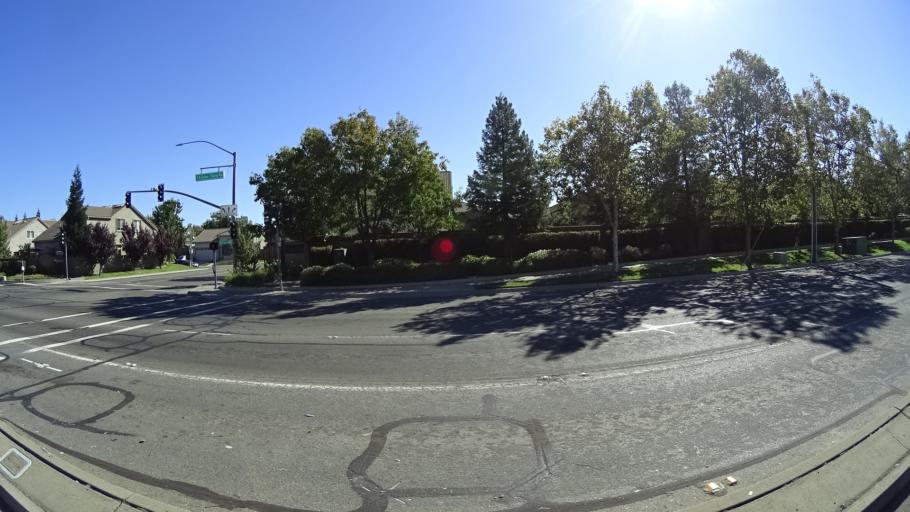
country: US
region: California
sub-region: Sacramento County
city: Vineyard
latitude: 38.4451
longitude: -121.3717
